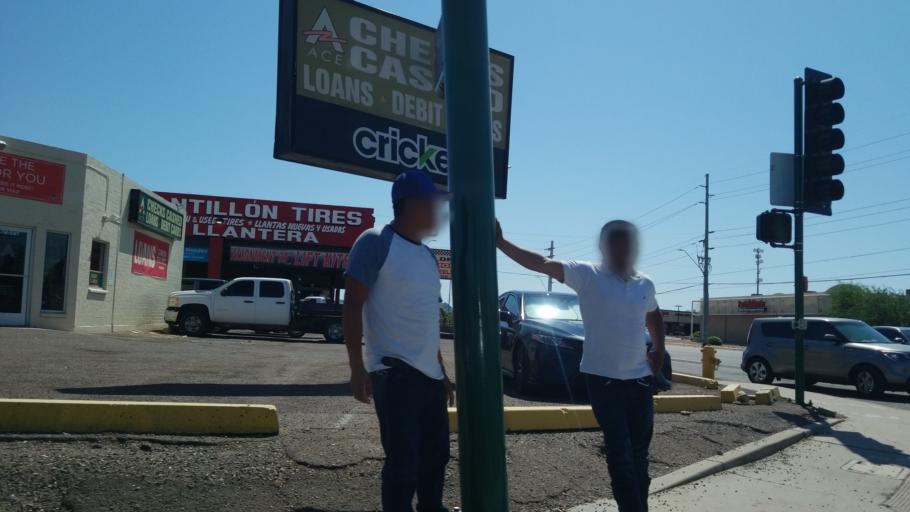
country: US
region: Arizona
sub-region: Maricopa County
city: Paradise Valley
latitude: 33.6271
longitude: -112.0155
